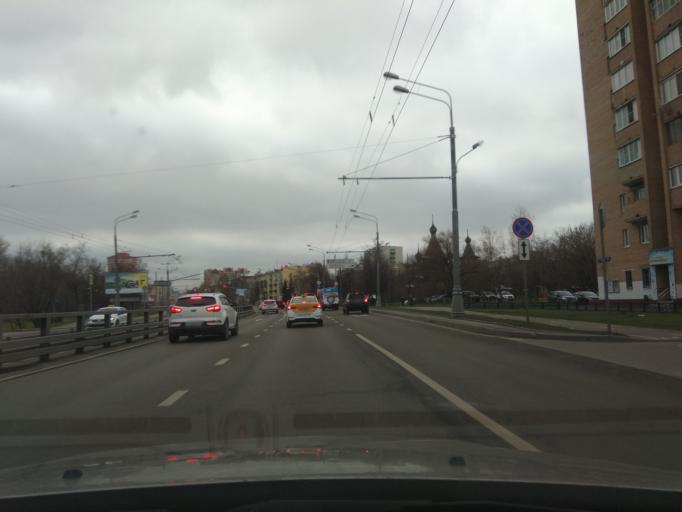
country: RU
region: Moskovskaya
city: Koptevo
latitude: 55.8315
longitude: 37.5316
